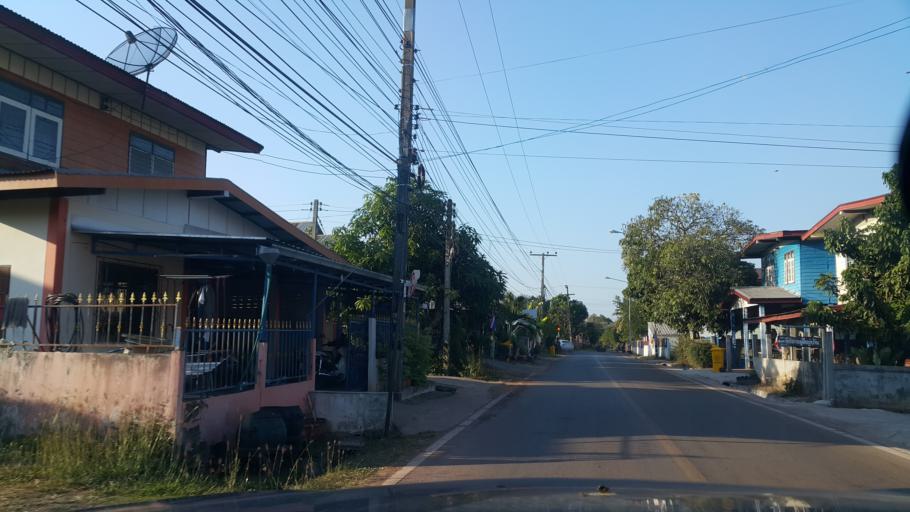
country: TH
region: Changwat Udon Thani
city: Ban Na Muang
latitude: 17.2660
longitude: 103.0043
